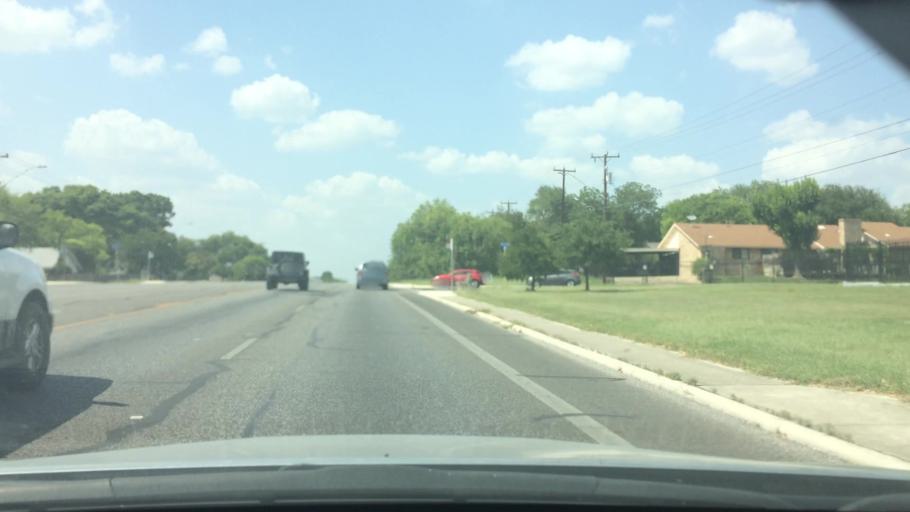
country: US
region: Texas
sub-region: Bexar County
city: Castle Hills
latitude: 29.5319
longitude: -98.5058
